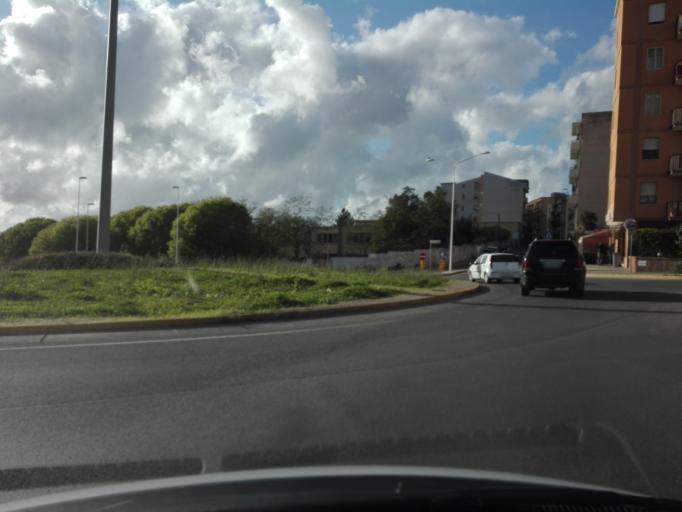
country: IT
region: Sardinia
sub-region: Provincia di Sassari
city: Sassari
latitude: 40.7324
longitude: 8.5696
